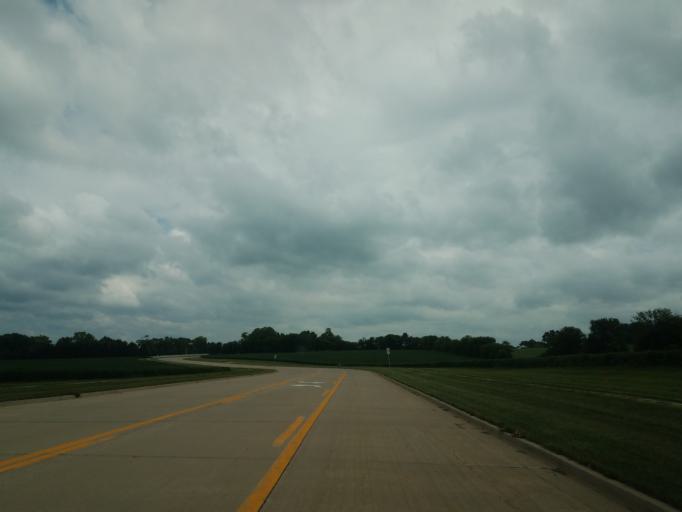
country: US
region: Illinois
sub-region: McLean County
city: Twin Grove
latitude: 40.4403
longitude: -89.0489
